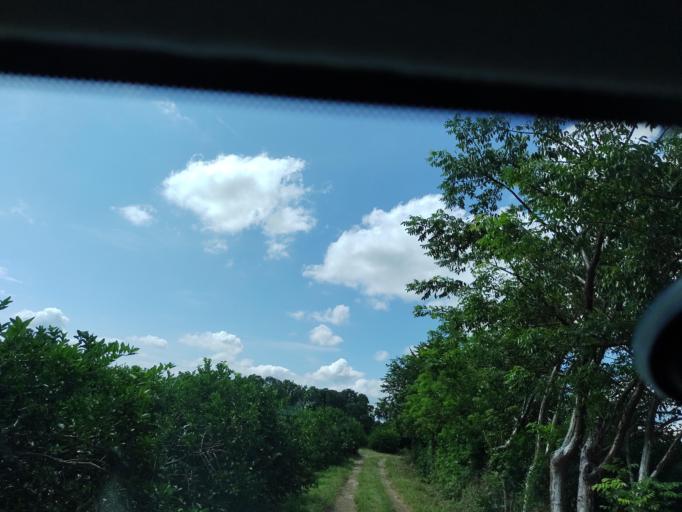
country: MX
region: Veracruz
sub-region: Martinez de la Torre
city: El Progreso
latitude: 20.1139
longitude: -97.0048
